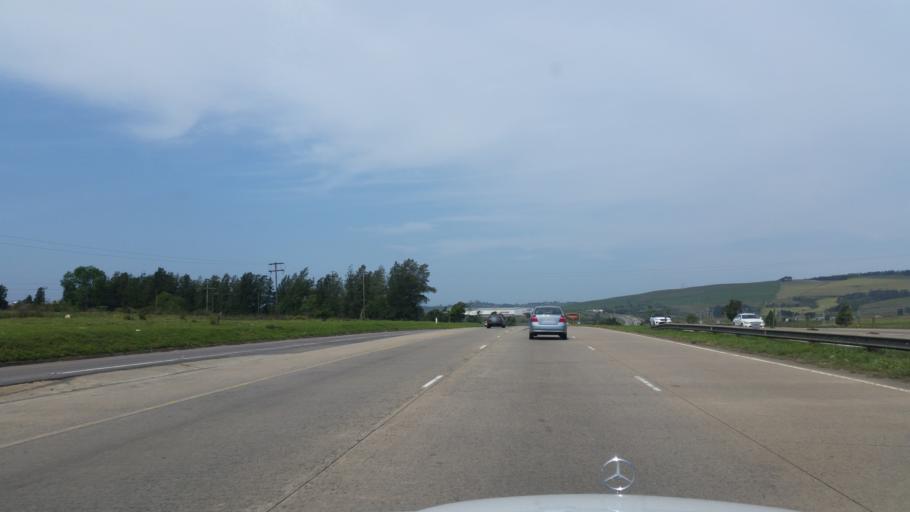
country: ZA
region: KwaZulu-Natal
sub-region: uMgungundlovu District Municipality
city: Camperdown
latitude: -29.7374
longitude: 30.6076
